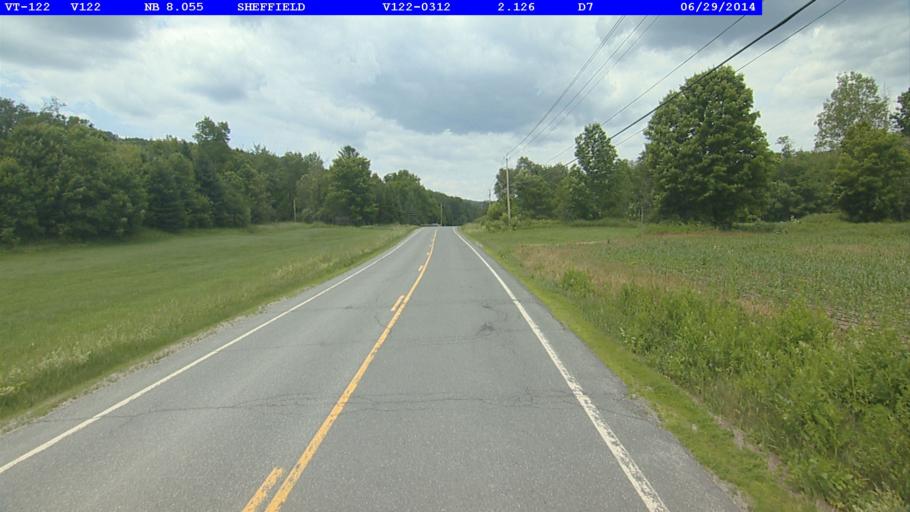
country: US
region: Vermont
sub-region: Caledonia County
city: Lyndonville
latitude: 44.6104
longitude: -72.1213
